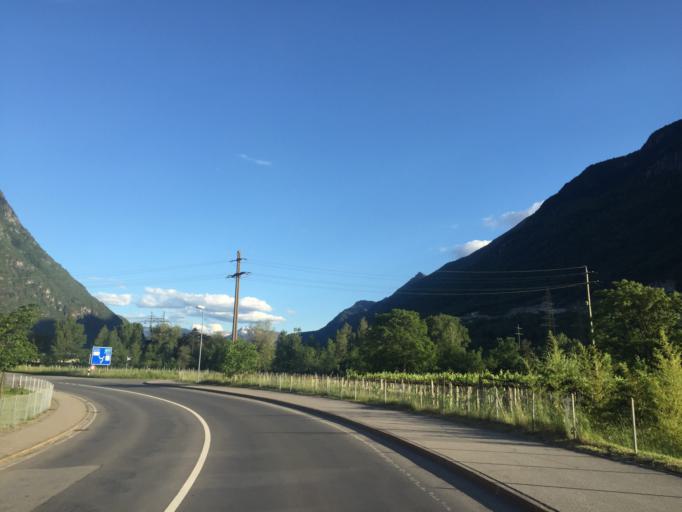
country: CH
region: Ticino
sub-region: Riviera District
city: Biasca
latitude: 46.3598
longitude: 8.9558
